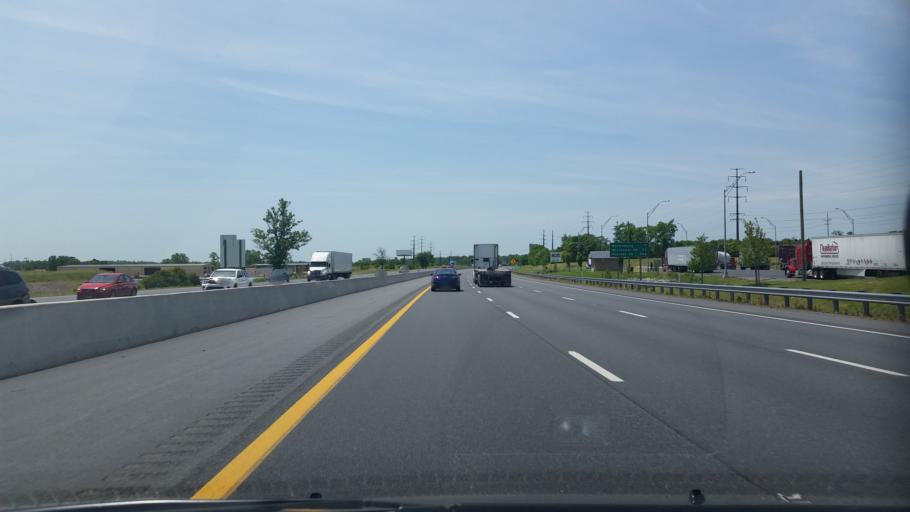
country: US
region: West Virginia
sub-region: Berkeley County
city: Martinsburg
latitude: 39.5371
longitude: -77.9171
